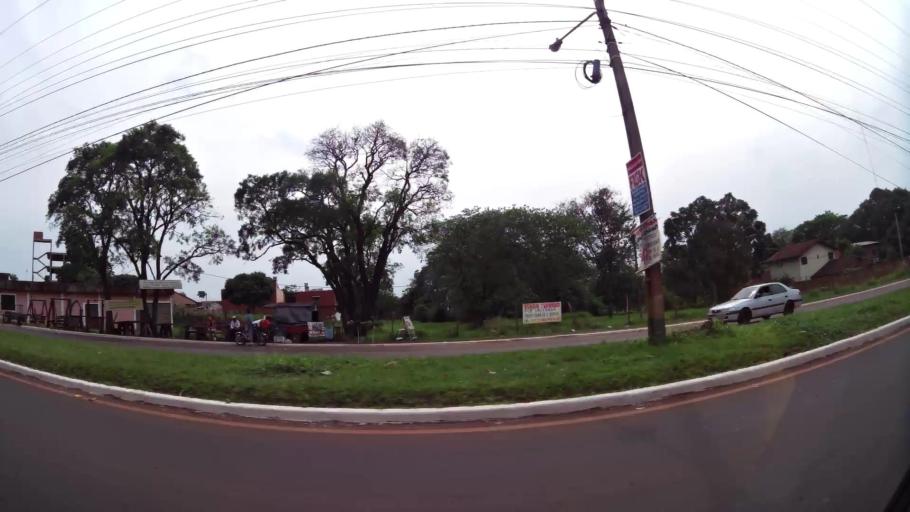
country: PY
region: Alto Parana
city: Presidente Franco
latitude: -25.5476
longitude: -54.6294
